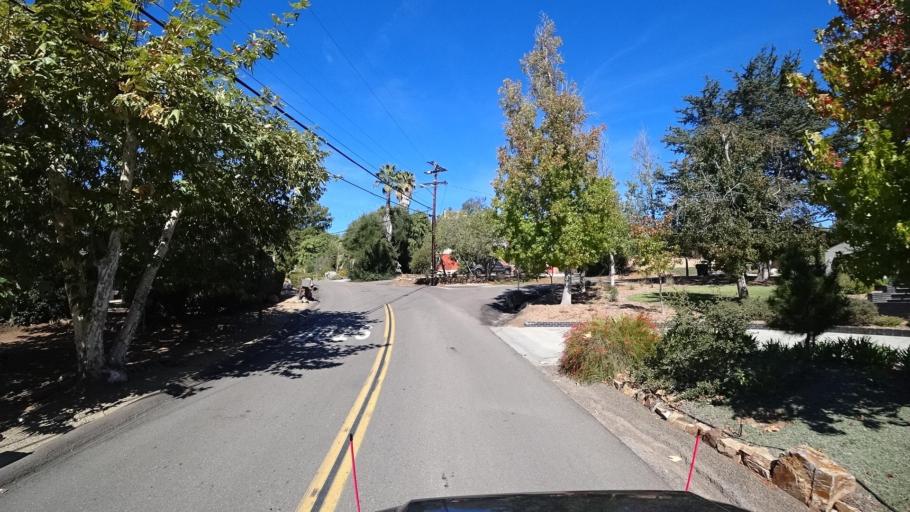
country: US
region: California
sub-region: San Diego County
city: Casa de Oro-Mount Helix
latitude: 32.7562
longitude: -116.9679
